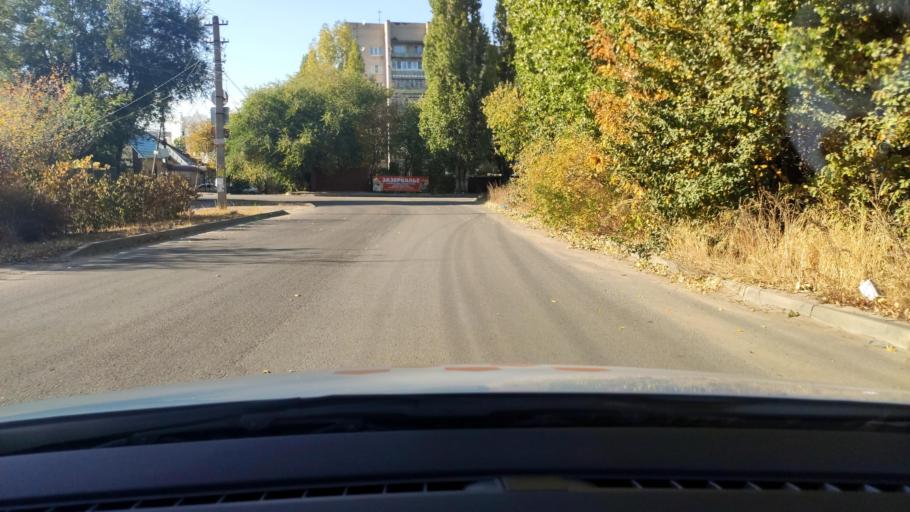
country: RU
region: Voronezj
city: Voronezh
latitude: 51.6834
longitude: 39.1437
